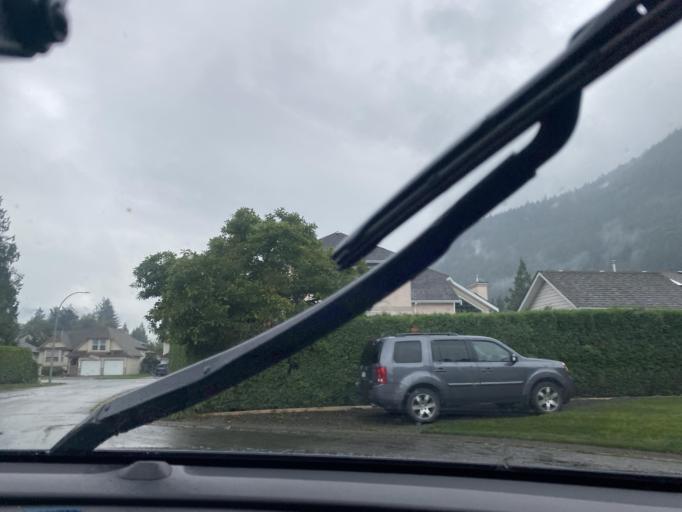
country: CA
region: British Columbia
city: Agassiz
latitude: 49.2970
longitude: -121.7817
